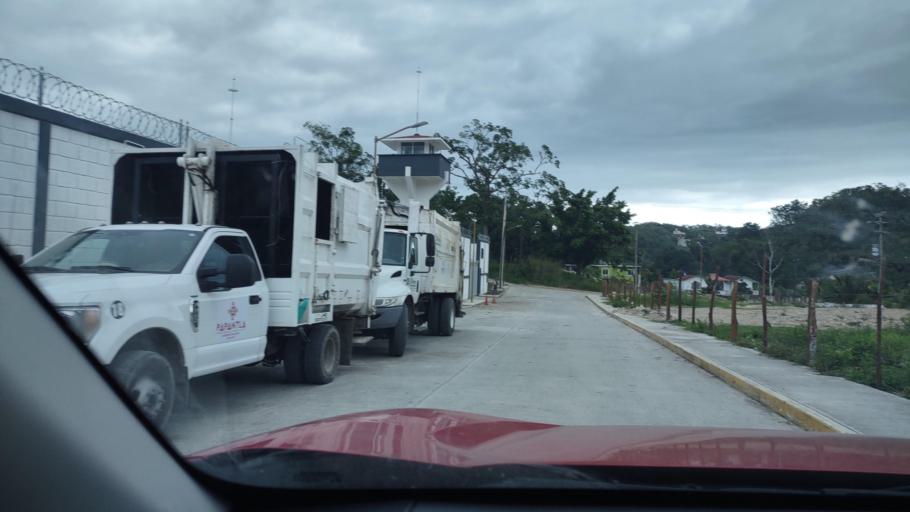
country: MX
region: Veracruz
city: Papantla de Olarte
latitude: 20.4398
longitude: -97.3422
